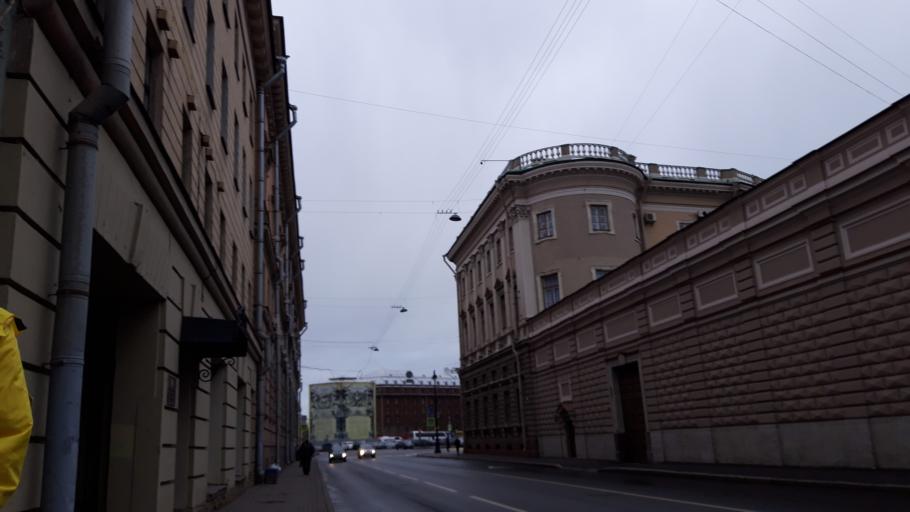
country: RU
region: St.-Petersburg
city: Saint Petersburg
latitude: 59.9301
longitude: 30.3083
